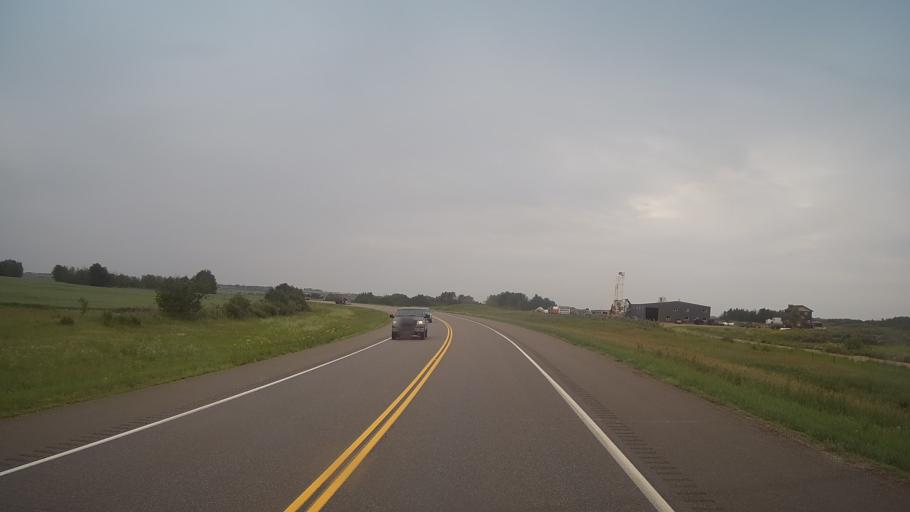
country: CA
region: Saskatchewan
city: Dalmeny
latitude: 52.1292
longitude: -106.8959
